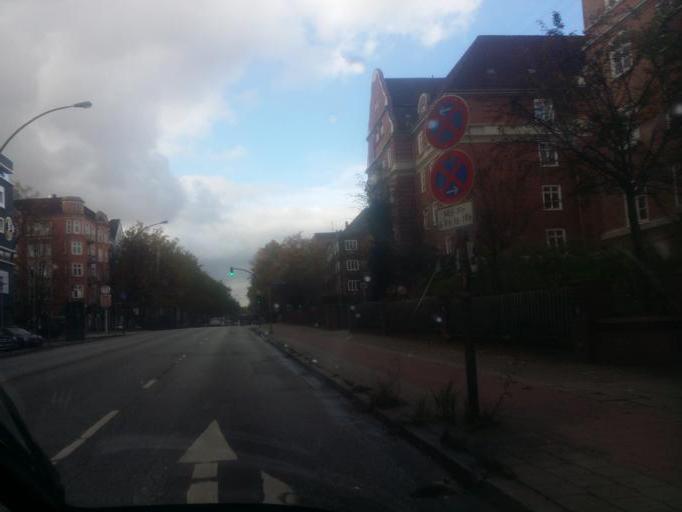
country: DE
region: Hamburg
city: Altona
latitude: 53.5634
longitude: 9.9306
